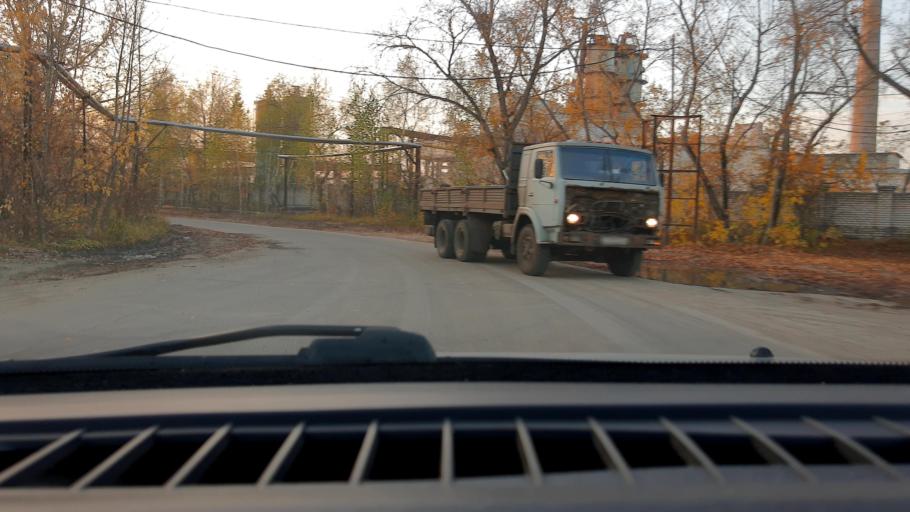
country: RU
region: Nizjnij Novgorod
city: Gorbatovka
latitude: 56.3750
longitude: 43.7882
